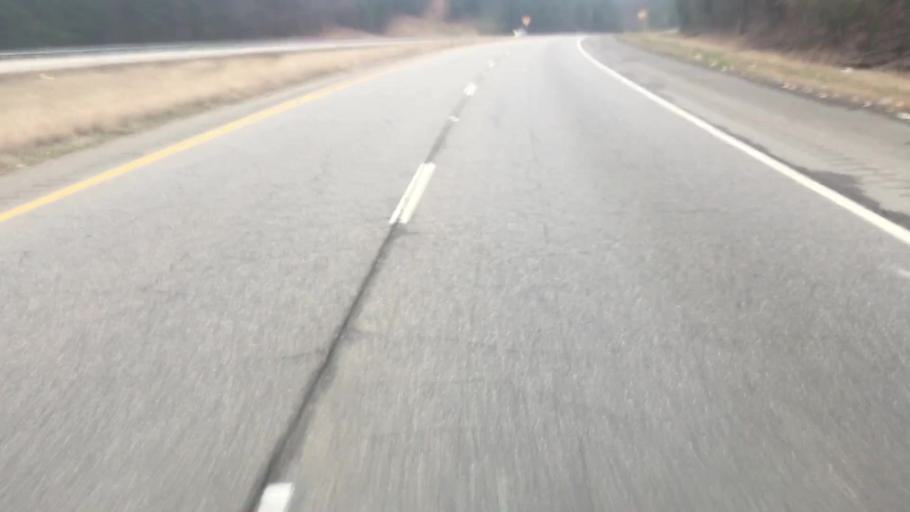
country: US
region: Alabama
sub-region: Walker County
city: Sumiton
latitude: 33.7729
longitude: -87.0737
